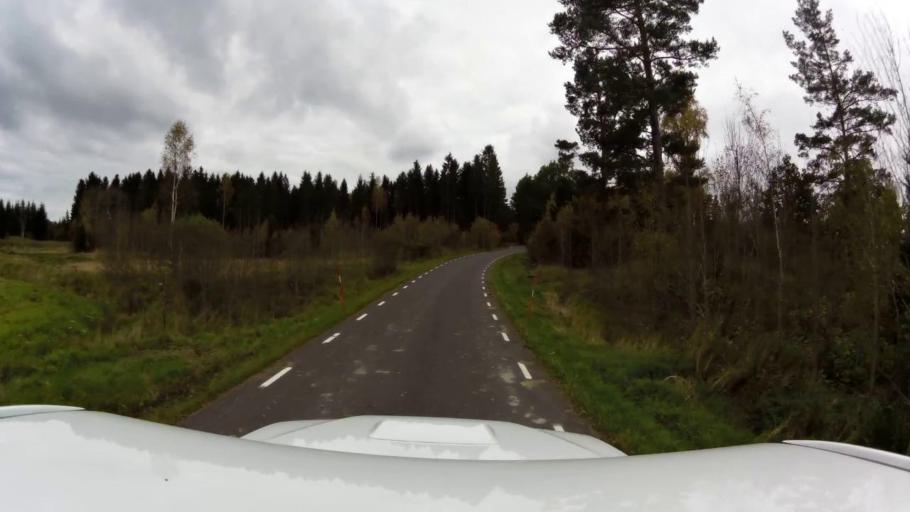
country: SE
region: OEstergoetland
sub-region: Linkopings Kommun
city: Ljungsbro
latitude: 58.5379
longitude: 15.4496
